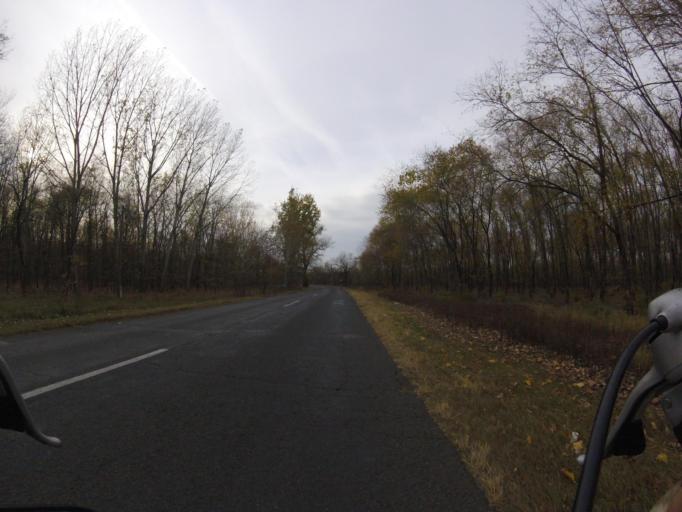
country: HU
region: Pest
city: Csemo
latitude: 47.1299
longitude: 19.6653
